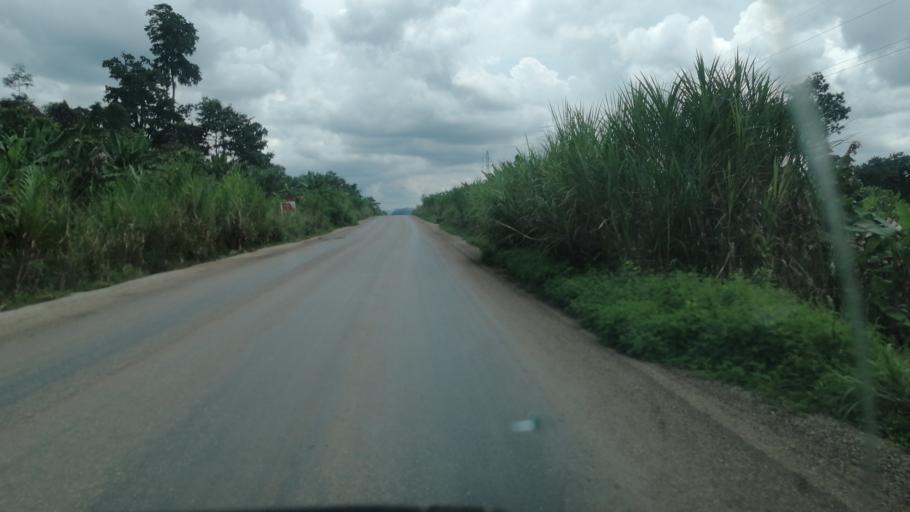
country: GH
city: Duayaw Nkwanta
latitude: 6.9085
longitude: -2.3948
